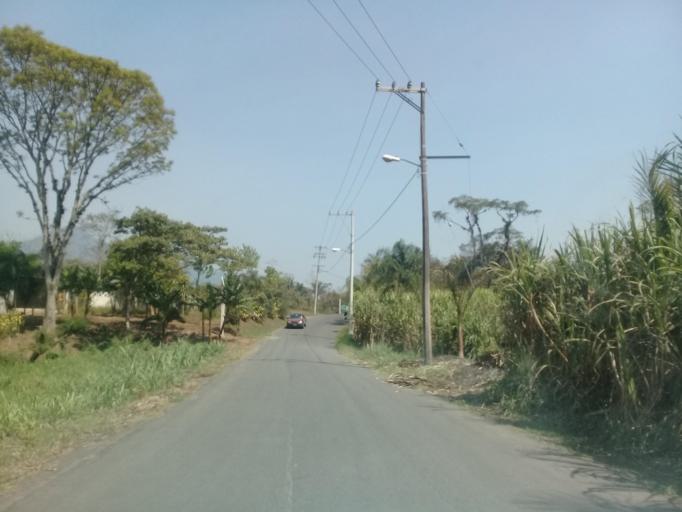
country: MX
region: Veracruz
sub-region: Ixtaczoquitlan
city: Capoluca
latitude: 18.8070
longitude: -96.9860
